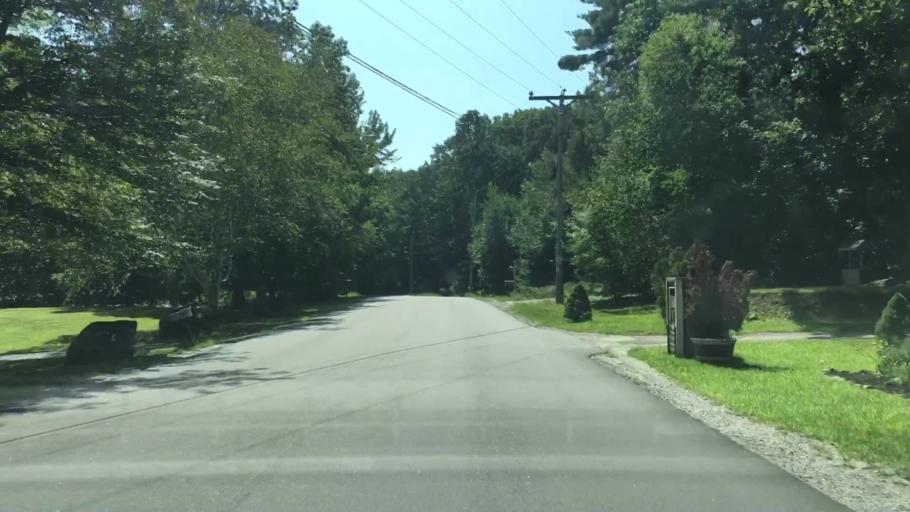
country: US
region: New Hampshire
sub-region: Rockingham County
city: Hampstead
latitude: 42.8899
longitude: -71.2177
